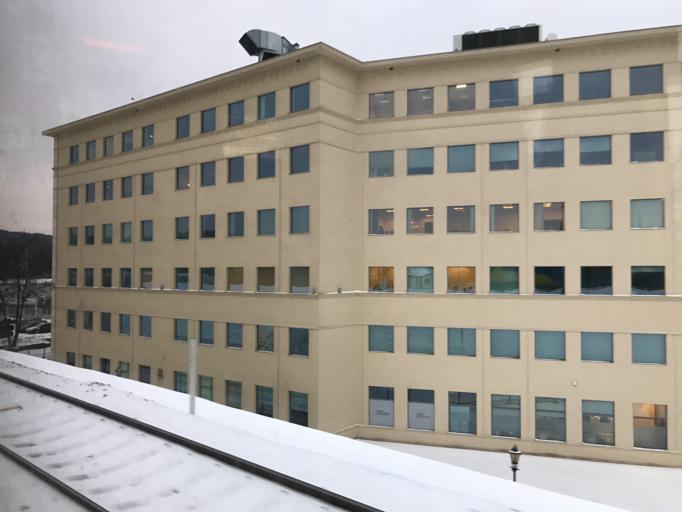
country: PL
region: Pomeranian Voivodeship
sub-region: Sopot
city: Sopot
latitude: 54.3922
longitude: 18.5809
